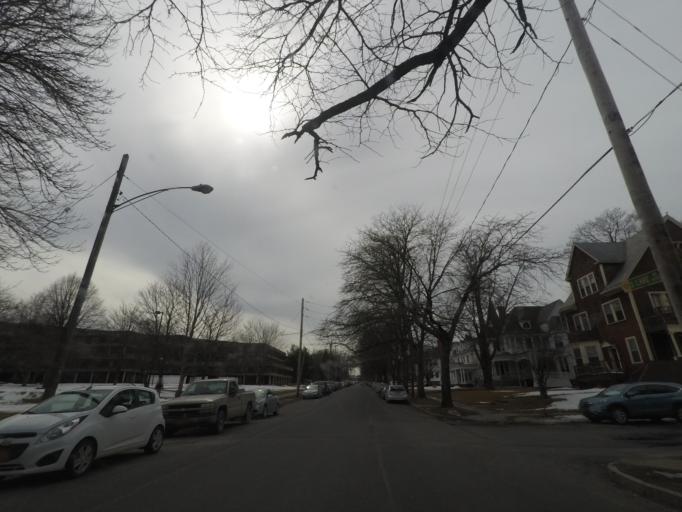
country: US
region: New York
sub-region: Albany County
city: Albany
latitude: 42.6558
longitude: -73.7797
